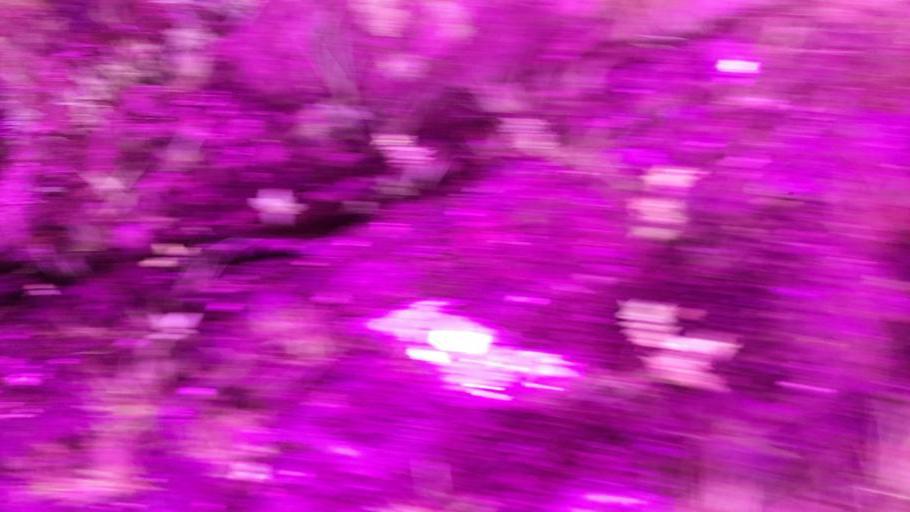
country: NP
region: Central Region
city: Kirtipur
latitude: 27.8308
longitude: 85.2043
